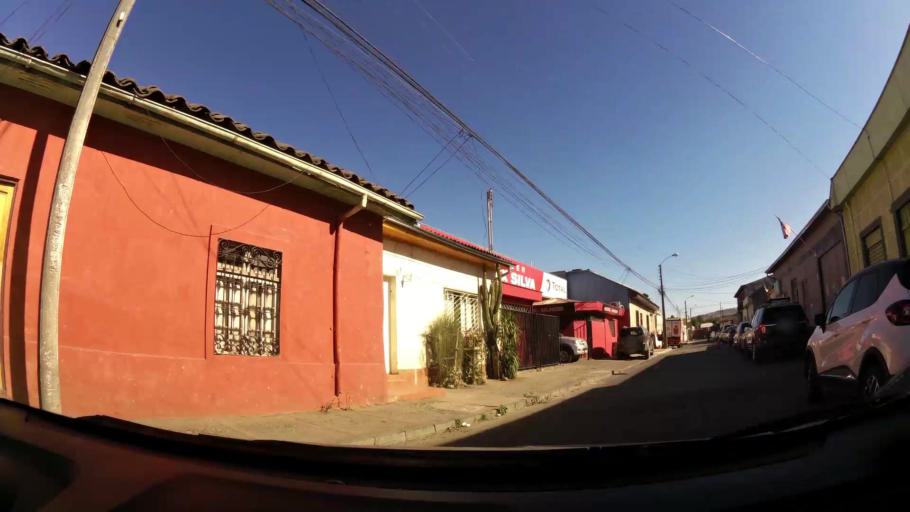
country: CL
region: O'Higgins
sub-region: Provincia de Colchagua
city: Chimbarongo
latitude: -34.5921
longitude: -70.9852
